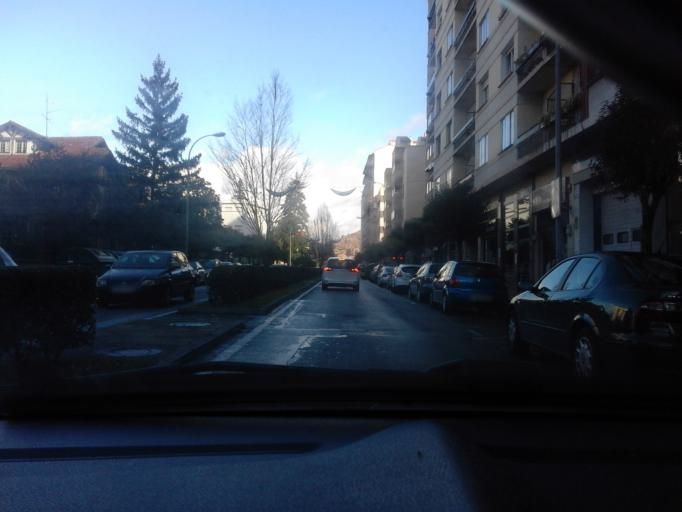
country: ES
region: Navarre
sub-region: Provincia de Navarra
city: Burlata
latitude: 42.8262
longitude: -1.6155
